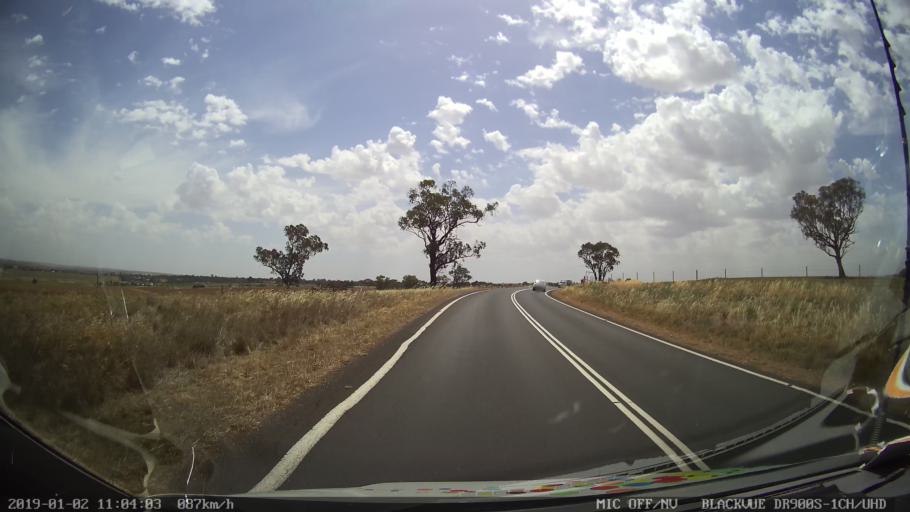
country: AU
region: New South Wales
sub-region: Young
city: Young
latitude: -34.5752
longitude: 148.3468
